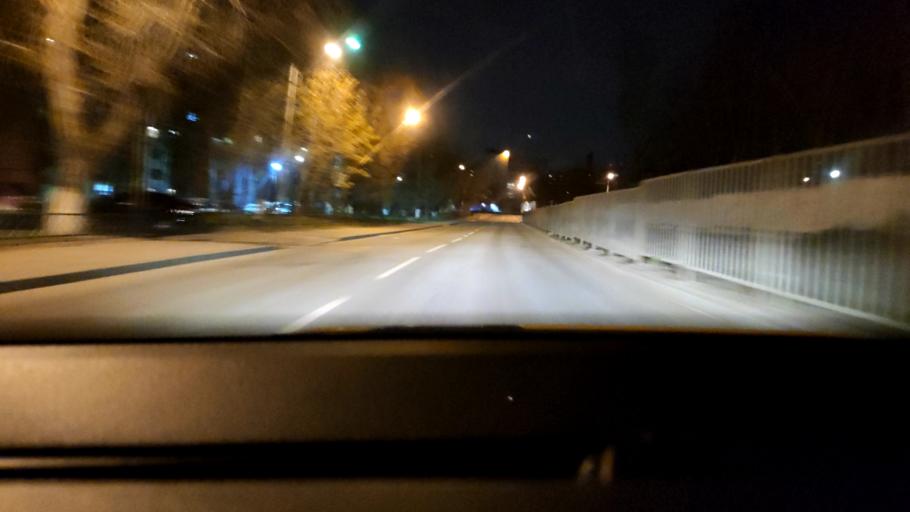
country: RU
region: Moskovskaya
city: Lyubertsy
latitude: 55.6722
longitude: 37.8811
